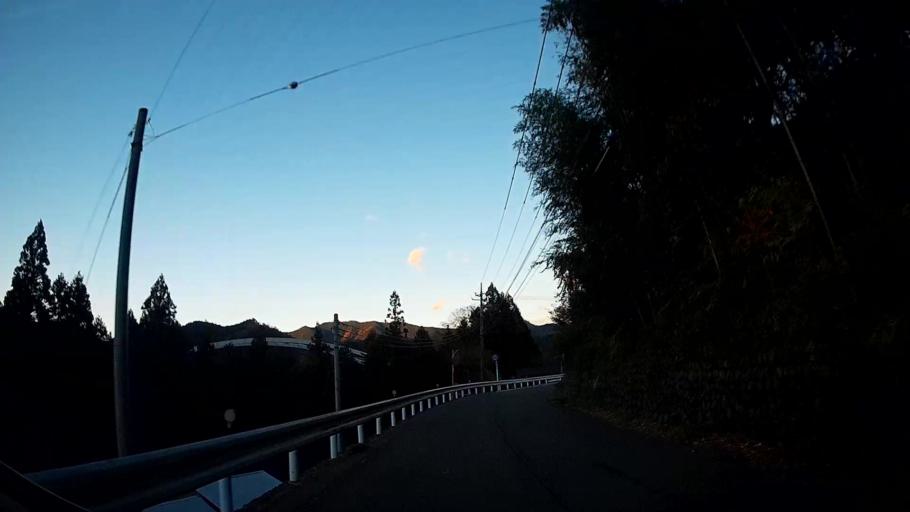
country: JP
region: Yamanashi
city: Uenohara
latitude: 35.5591
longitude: 139.1792
